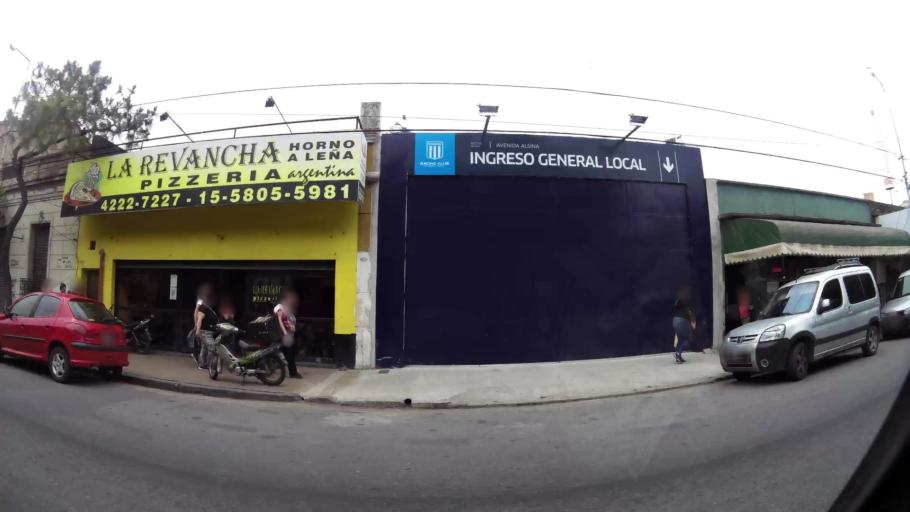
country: AR
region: Buenos Aires
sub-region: Partido de Avellaneda
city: Avellaneda
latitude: -34.6682
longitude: -58.3715
